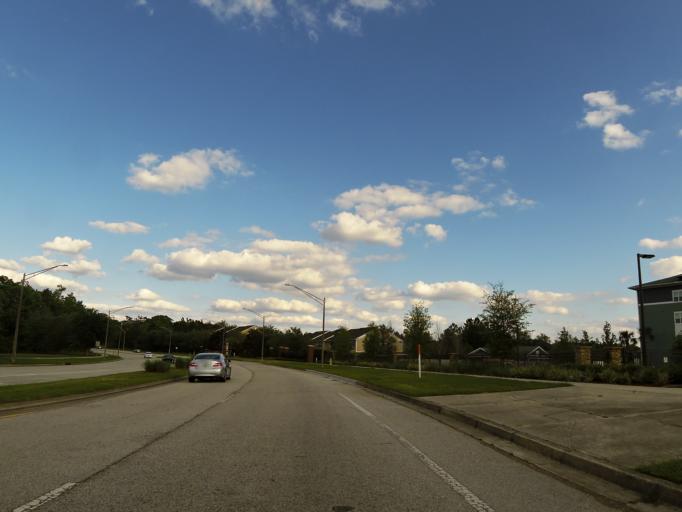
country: US
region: Florida
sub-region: Duval County
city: Jacksonville
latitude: 30.2544
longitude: -81.5785
